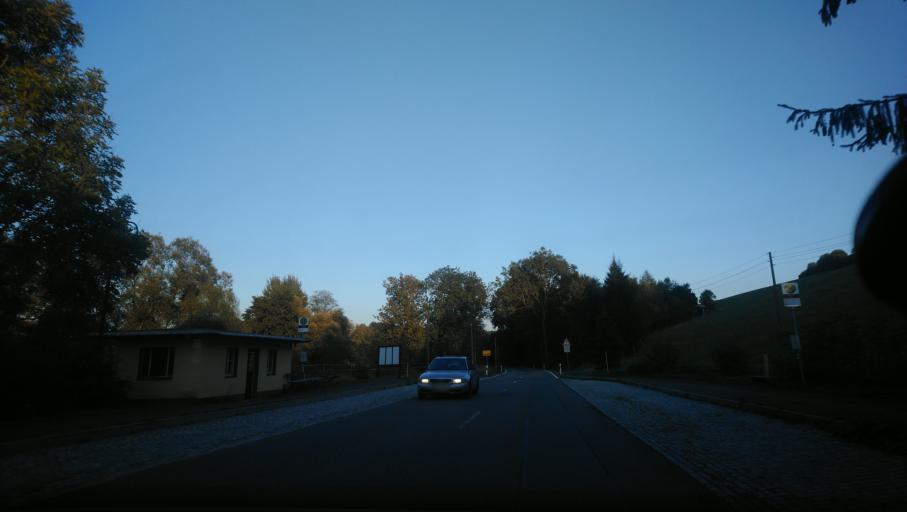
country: DE
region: Saxony
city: Tannenberg
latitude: 50.6092
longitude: 12.9636
